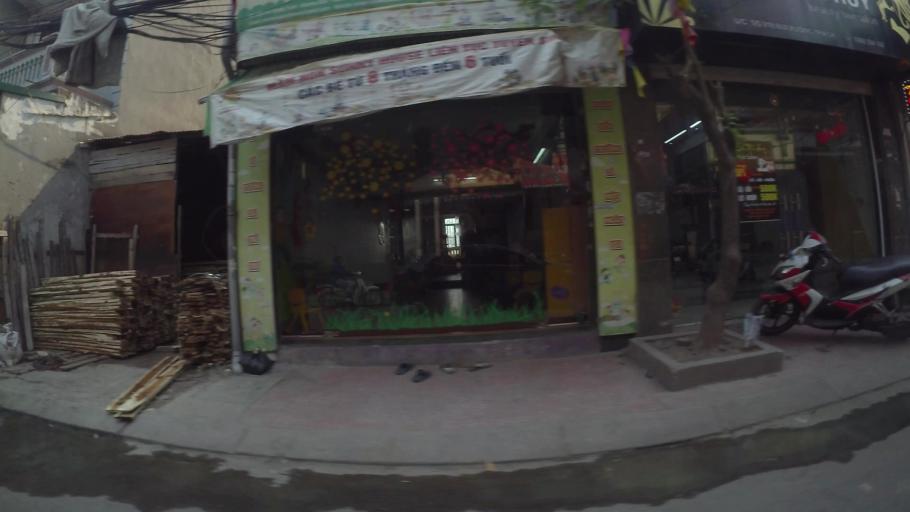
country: VN
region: Ha Noi
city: Thanh Xuan
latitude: 20.9878
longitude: 105.8184
